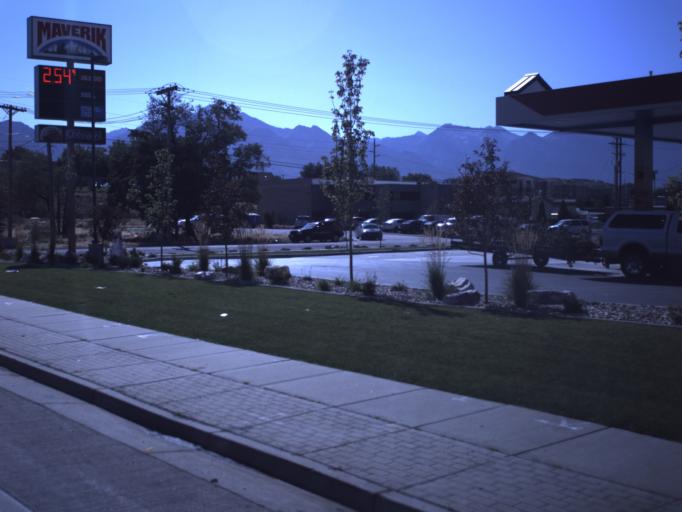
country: US
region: Utah
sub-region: Salt Lake County
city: Murray
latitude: 40.6744
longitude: -111.9003
